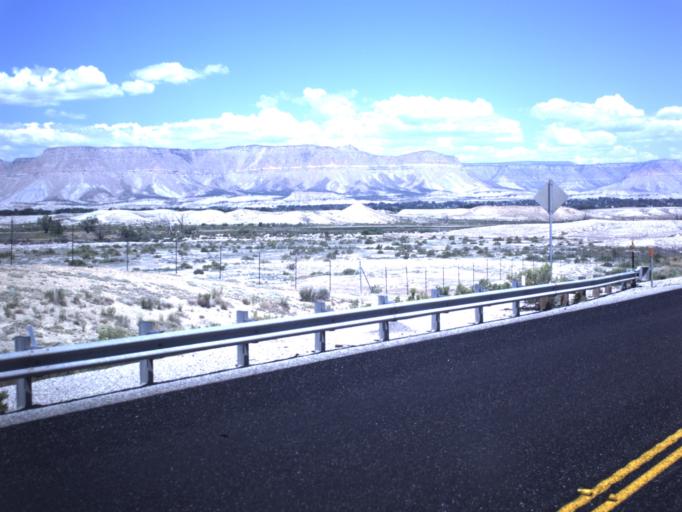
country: US
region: Utah
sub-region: Emery County
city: Ferron
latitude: 39.0477
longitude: -111.1228
